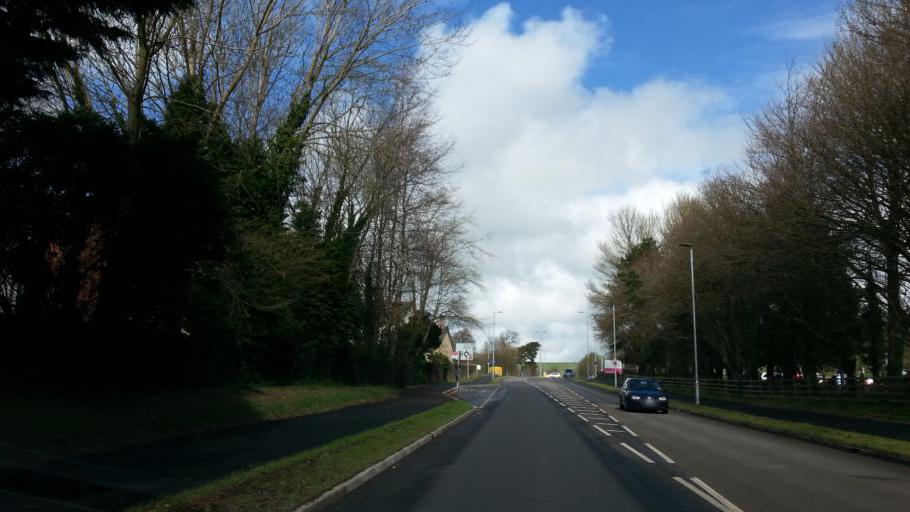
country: GB
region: England
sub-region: Devon
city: Barnstaple
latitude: 51.0914
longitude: -4.0534
